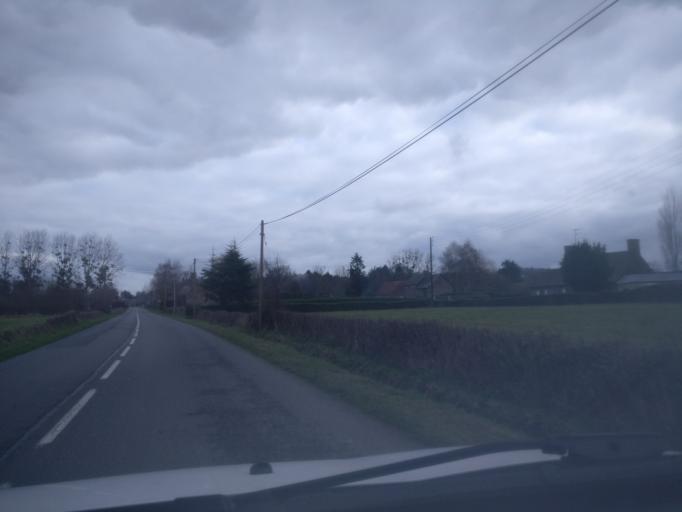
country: FR
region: Lower Normandy
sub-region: Departement de la Manche
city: Marcey-les-Greves
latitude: 48.6807
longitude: -1.3930
